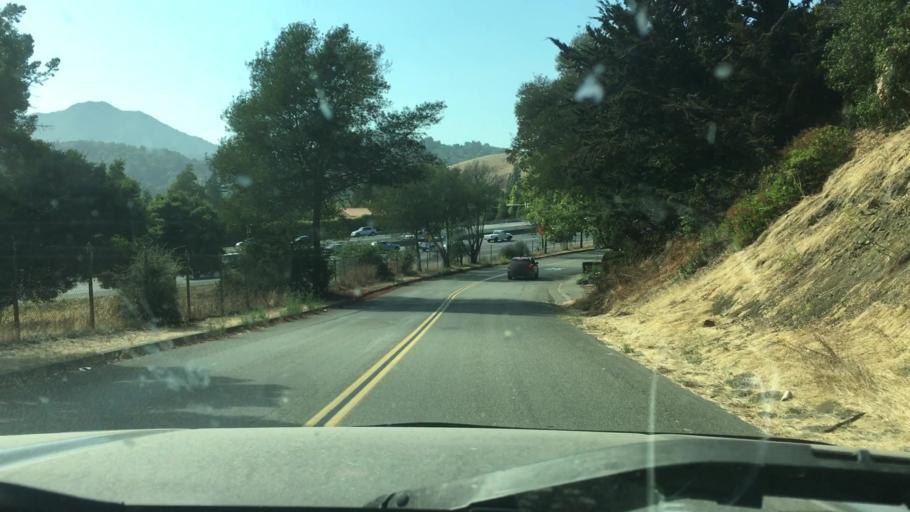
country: US
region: California
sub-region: Marin County
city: Strawberry
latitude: 37.9037
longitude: -122.5145
